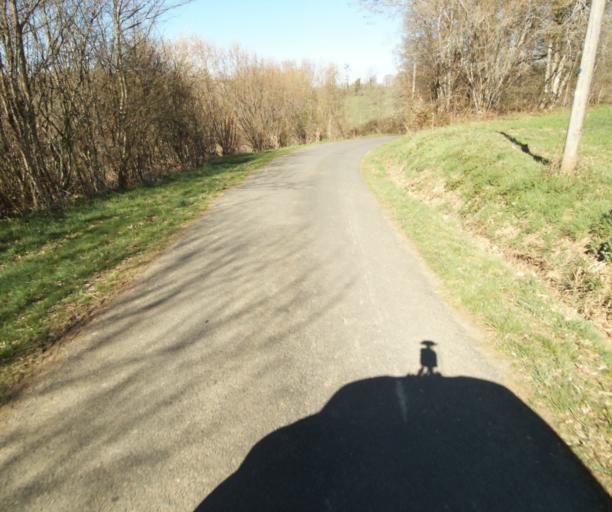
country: FR
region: Limousin
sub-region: Departement de la Correze
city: Chamboulive
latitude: 45.4112
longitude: 1.7240
